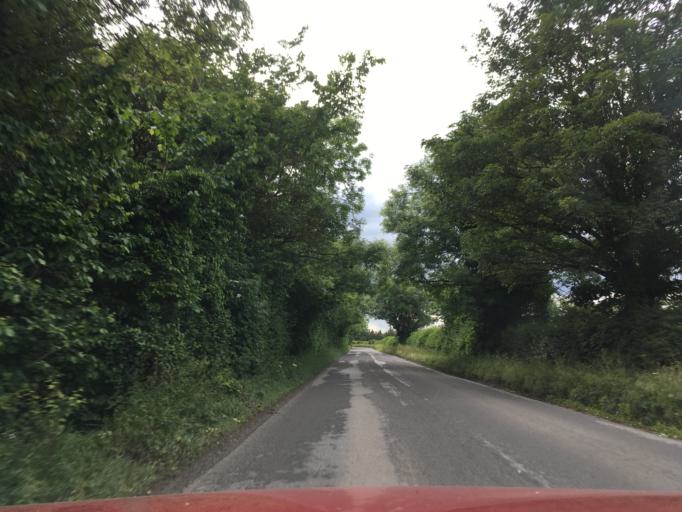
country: GB
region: England
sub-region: Wiltshire
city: Minety
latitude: 51.6561
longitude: -1.9503
